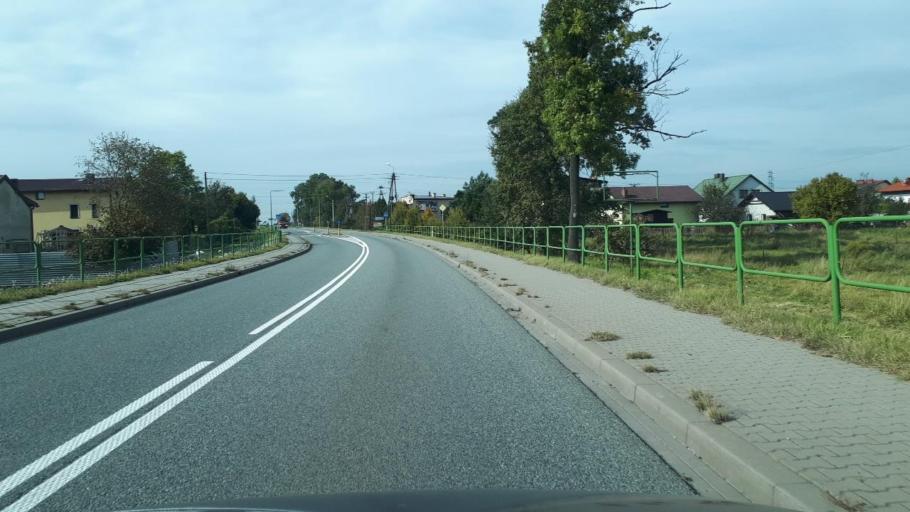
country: PL
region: Silesian Voivodeship
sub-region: Powiat pszczynski
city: Rudziczka
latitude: 50.0355
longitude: 18.7656
